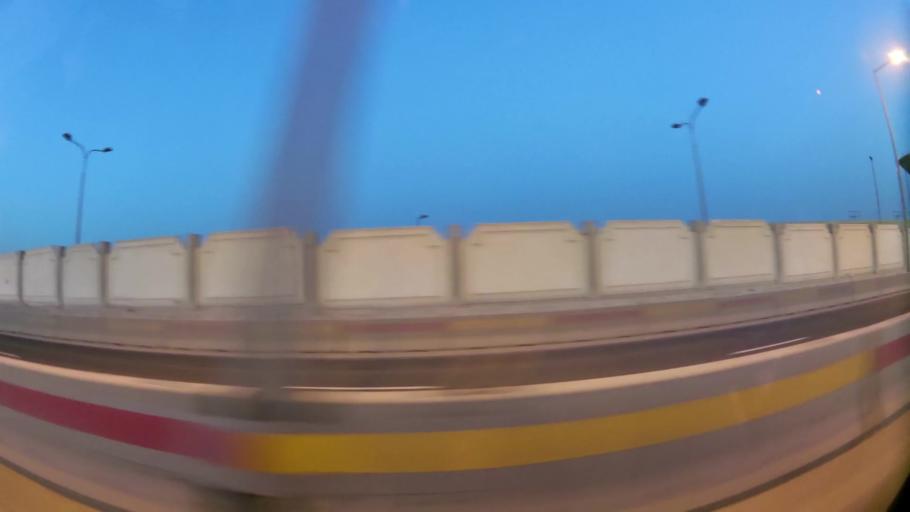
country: QA
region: Baladiyat ar Rayyan
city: Ar Rayyan
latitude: 25.3157
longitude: 51.4507
